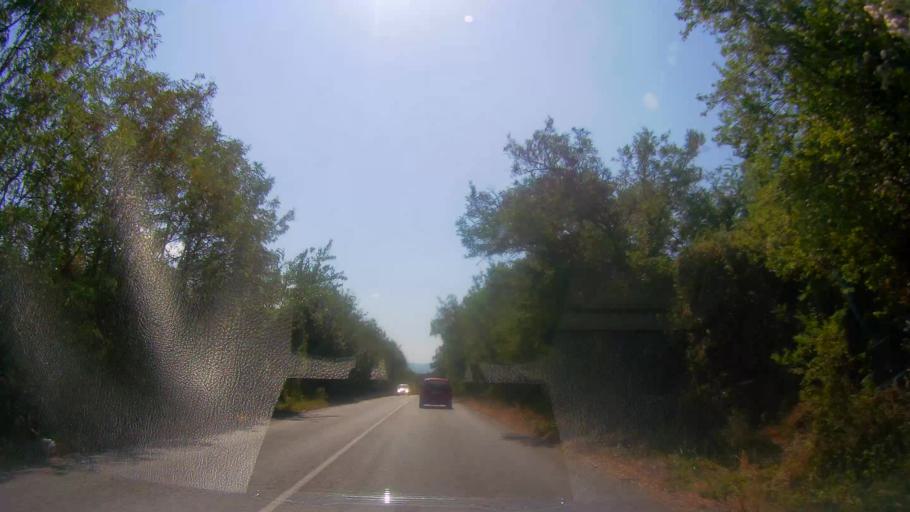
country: BG
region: Veliko Turnovo
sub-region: Obshtina Gorna Oryakhovitsa
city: Purvomaytsi
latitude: 43.2538
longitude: 25.6430
